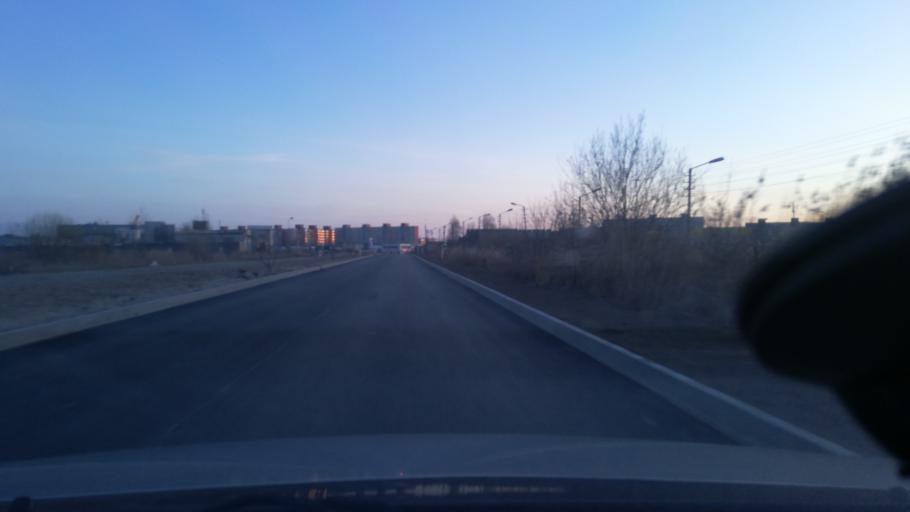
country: LT
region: Klaipedos apskritis
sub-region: Klaipeda
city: Klaipeda
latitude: 55.6808
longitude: 21.1945
